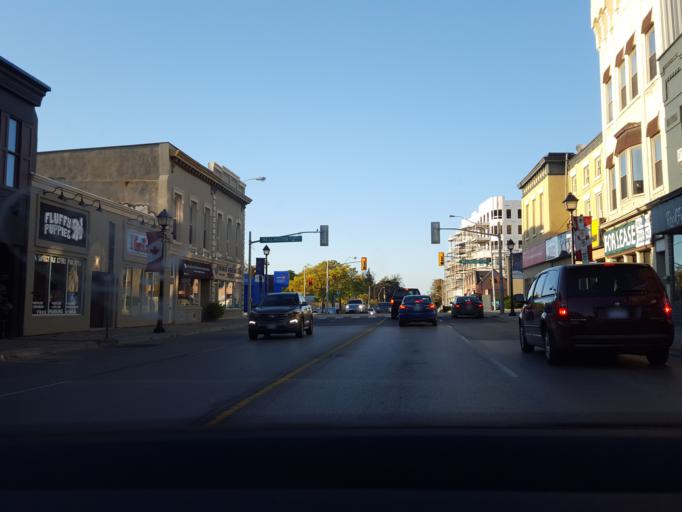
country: CA
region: Ontario
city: Newmarket
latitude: 43.9992
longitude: -79.4674
